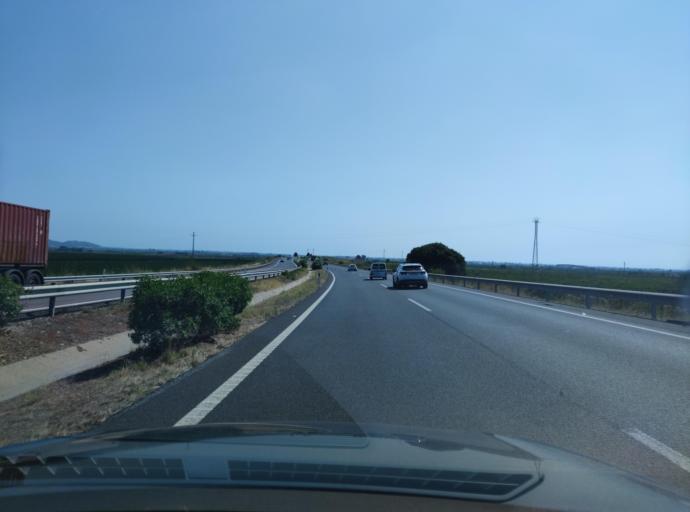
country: ES
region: Valencia
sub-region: Provincia de Valencia
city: Faura
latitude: 39.7021
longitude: -0.2585
